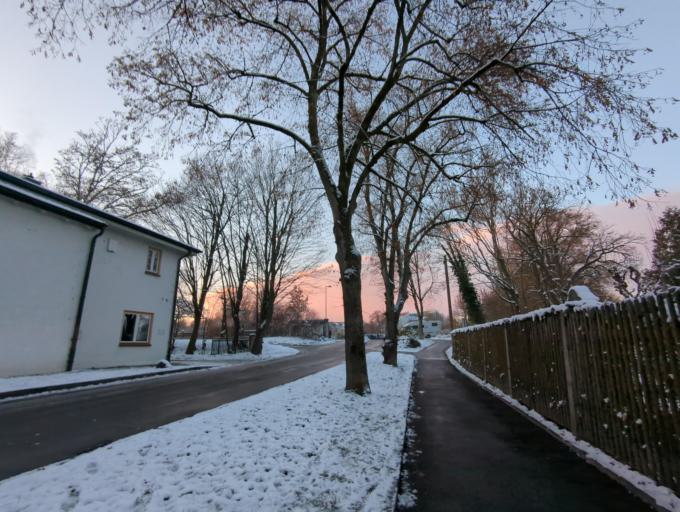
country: DE
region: Bavaria
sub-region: Upper Bavaria
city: Landsberg am Lech
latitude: 48.0552
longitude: 10.8740
